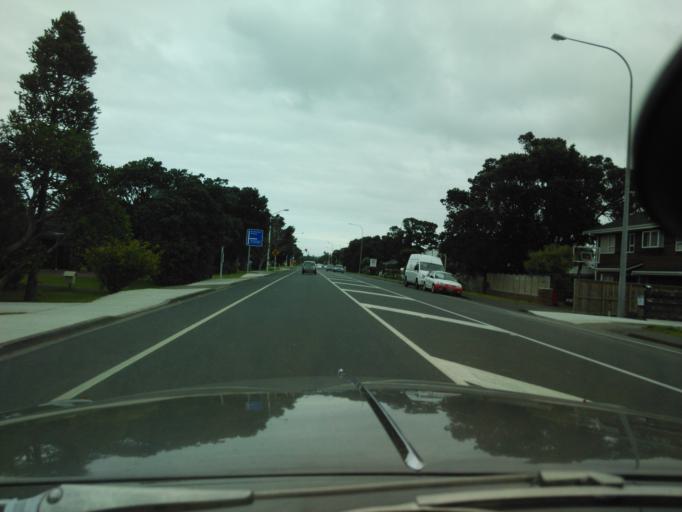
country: NZ
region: Auckland
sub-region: Auckland
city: Rothesay Bay
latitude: -36.5787
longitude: 174.6921
